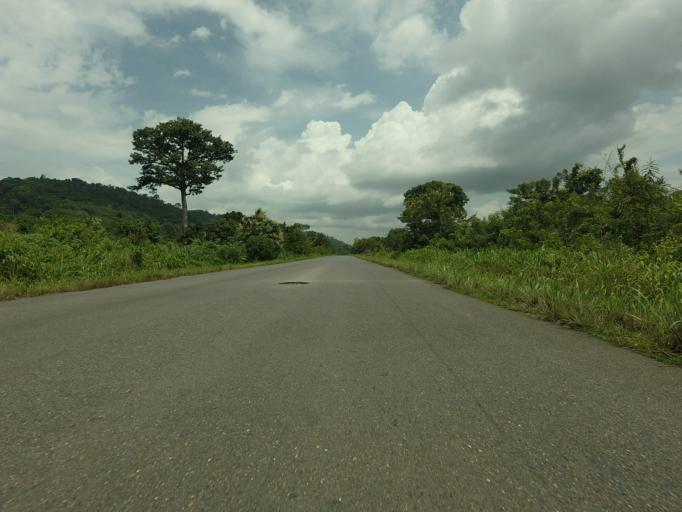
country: GH
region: Volta
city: Ho
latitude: 6.4879
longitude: 0.1992
